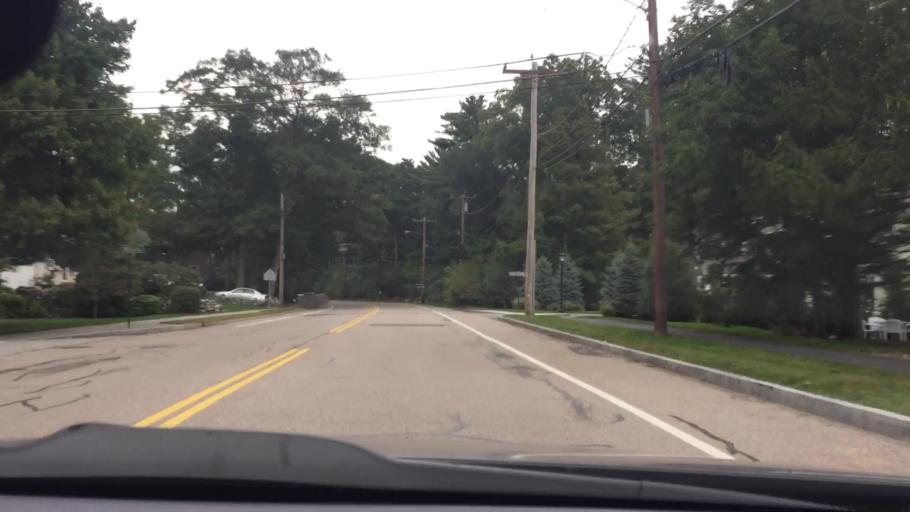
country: US
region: Massachusetts
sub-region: Norfolk County
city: Needham
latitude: 42.2784
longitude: -71.2041
